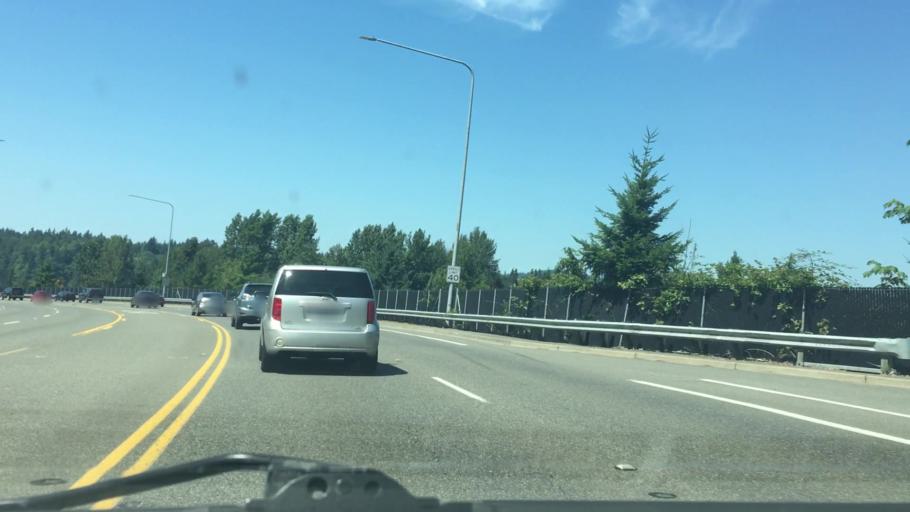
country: US
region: Washington
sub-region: King County
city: Fairwood
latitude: 47.4614
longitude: -122.1472
